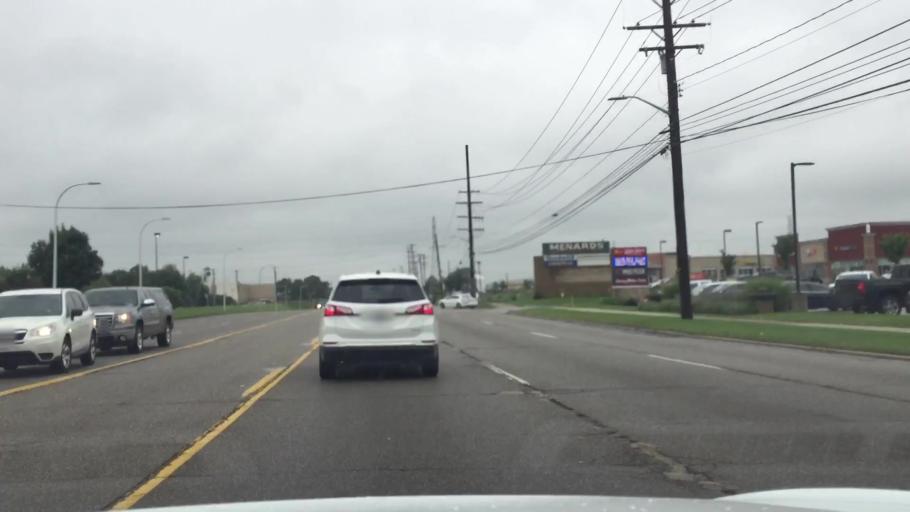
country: US
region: Michigan
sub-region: Wayne County
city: Livonia
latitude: 42.3797
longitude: -83.3336
